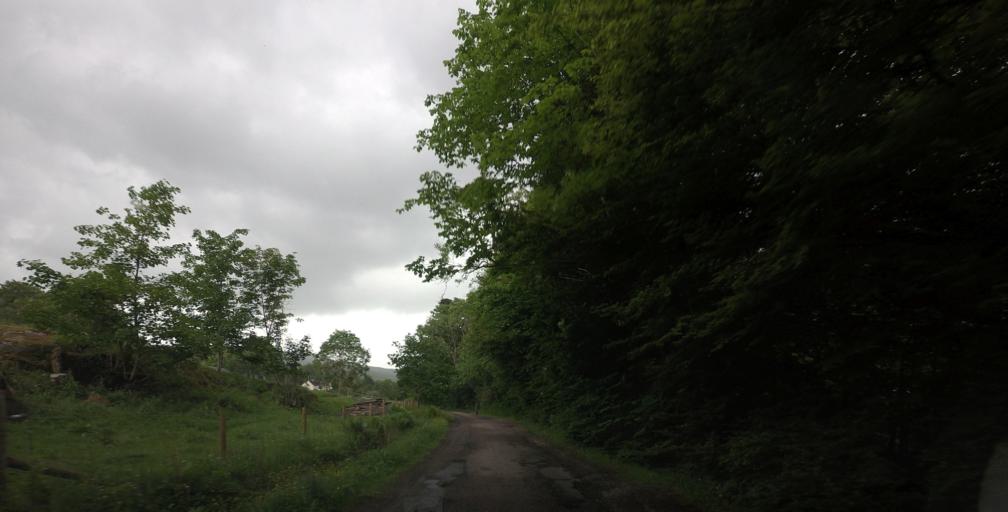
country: GB
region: Scotland
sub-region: Argyll and Bute
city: Oban
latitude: 56.6986
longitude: -5.5710
